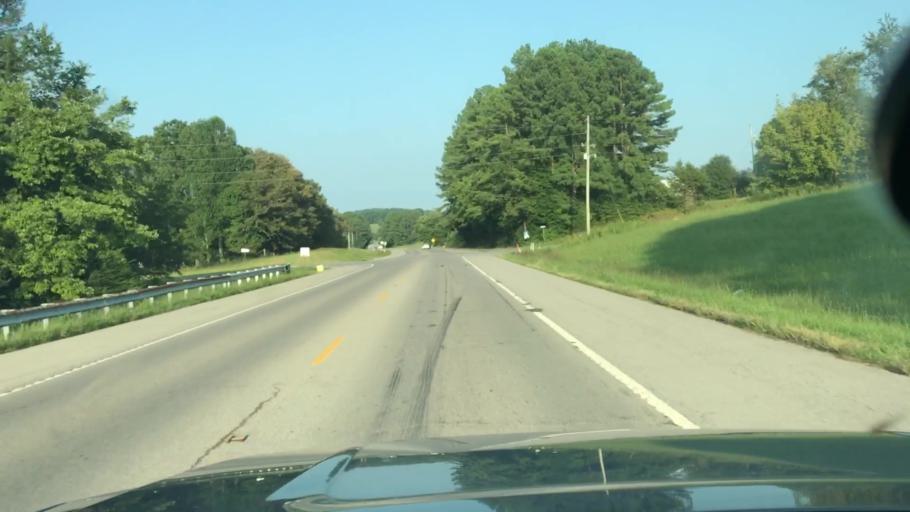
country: US
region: Tennessee
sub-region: Sumner County
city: Portland
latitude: 36.5788
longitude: -86.4272
